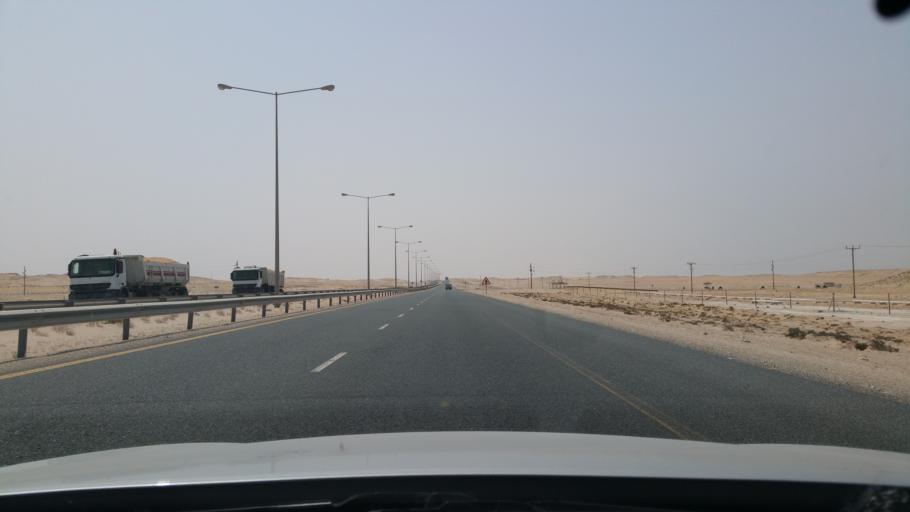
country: QA
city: Umm Bab
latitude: 25.1801
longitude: 50.8094
